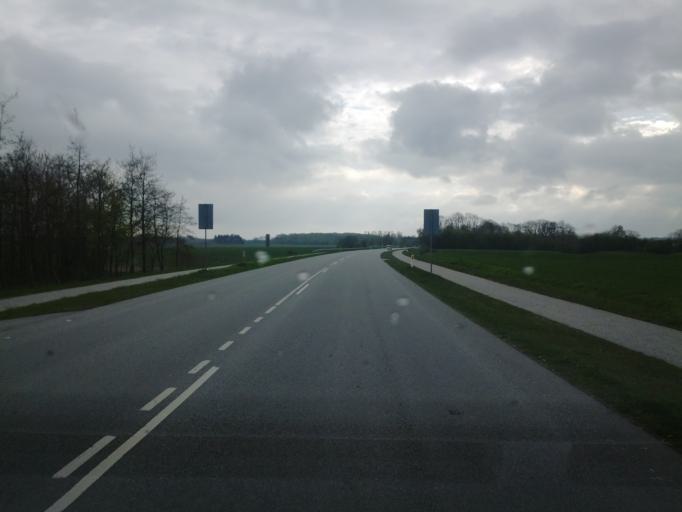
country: DK
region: North Denmark
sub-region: Frederikshavn Kommune
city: Saeby
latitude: 57.3052
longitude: 10.4267
